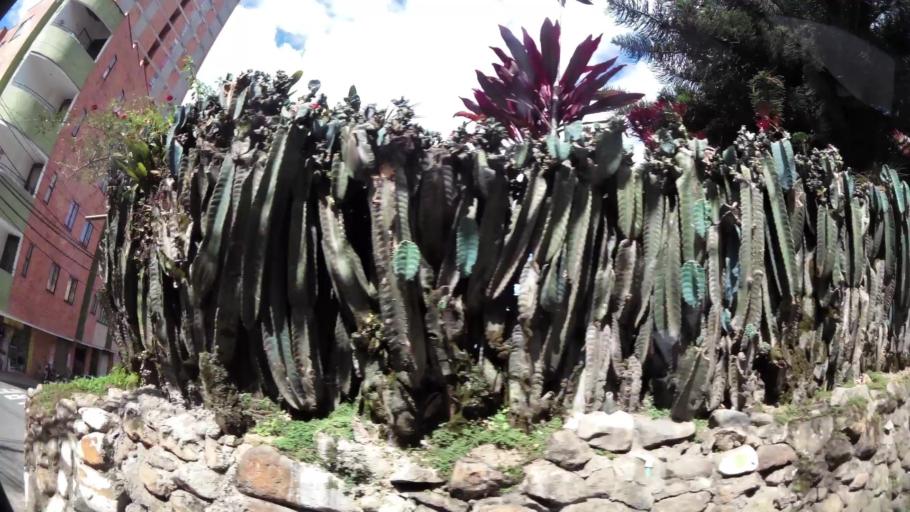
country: CO
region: Antioquia
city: Sabaneta
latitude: 6.1548
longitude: -75.6040
